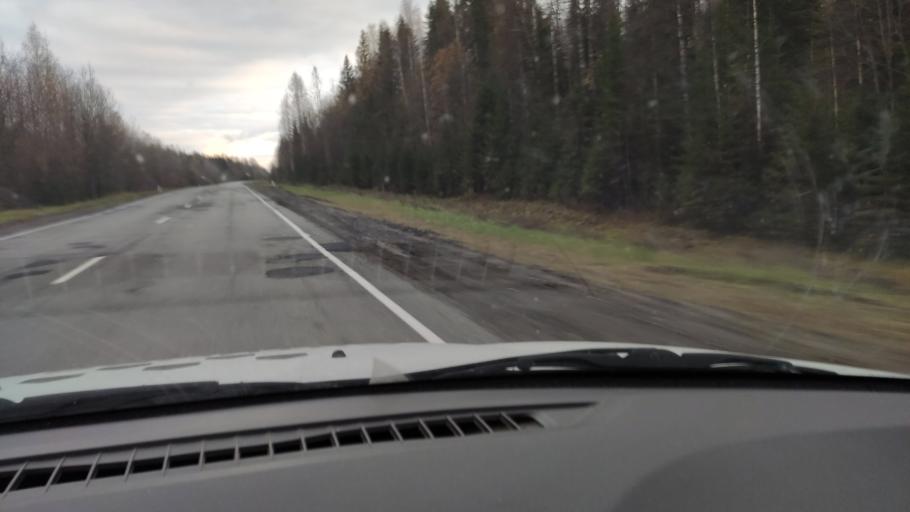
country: RU
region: Kirov
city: Omutninsk
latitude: 58.7552
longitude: 52.0398
